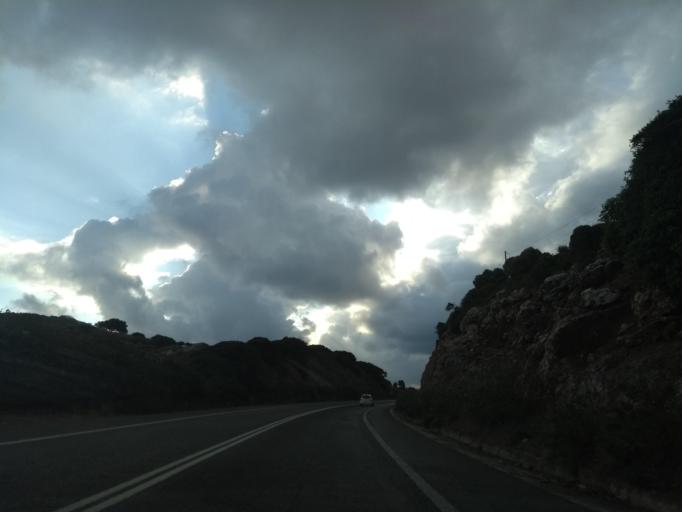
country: GR
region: Crete
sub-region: Nomos Rethymnis
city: Zoniana
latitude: 35.4088
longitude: 24.8223
